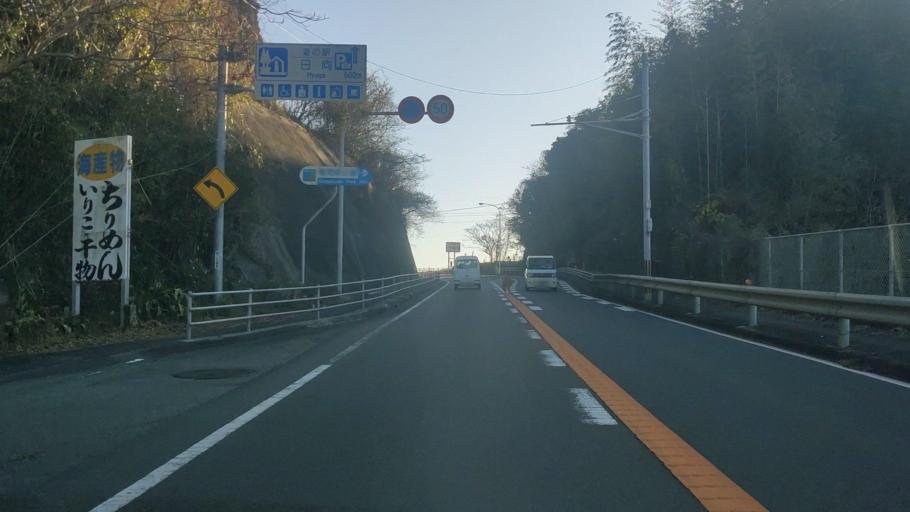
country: JP
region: Miyazaki
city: Takanabe
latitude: 32.3415
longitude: 131.6166
